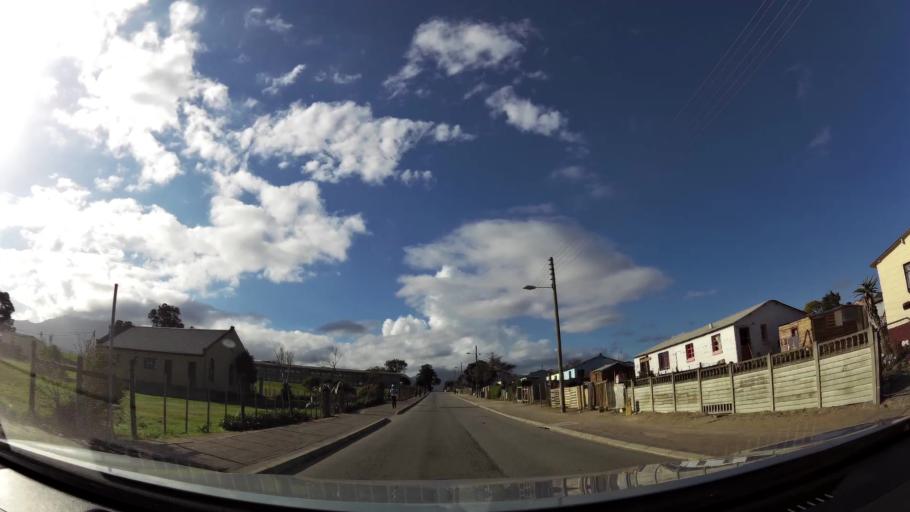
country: ZA
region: Western Cape
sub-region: Eden District Municipality
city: George
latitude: -33.9773
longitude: 22.4780
